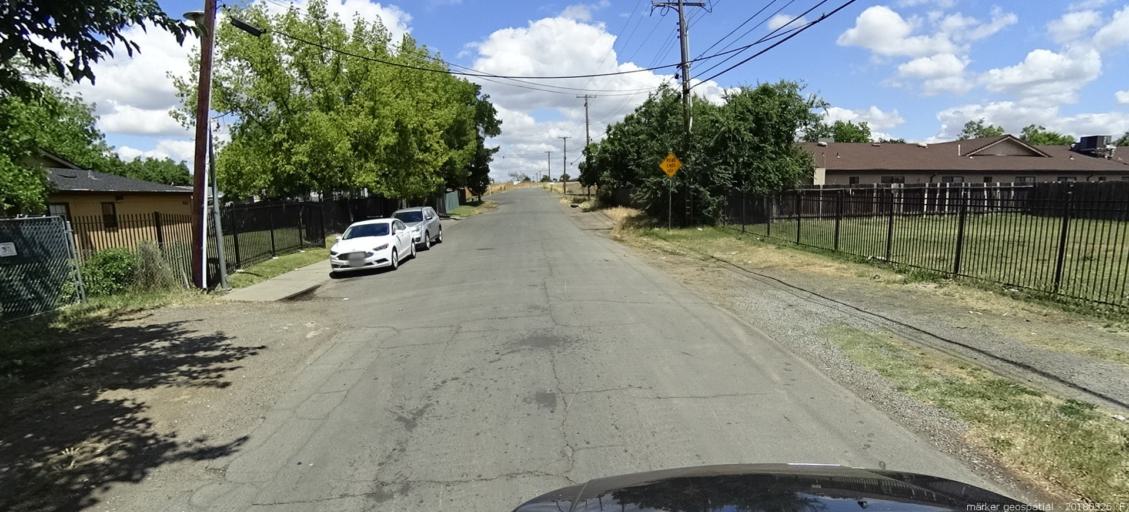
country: US
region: California
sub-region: Sacramento County
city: Sacramento
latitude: 38.6303
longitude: -121.4729
